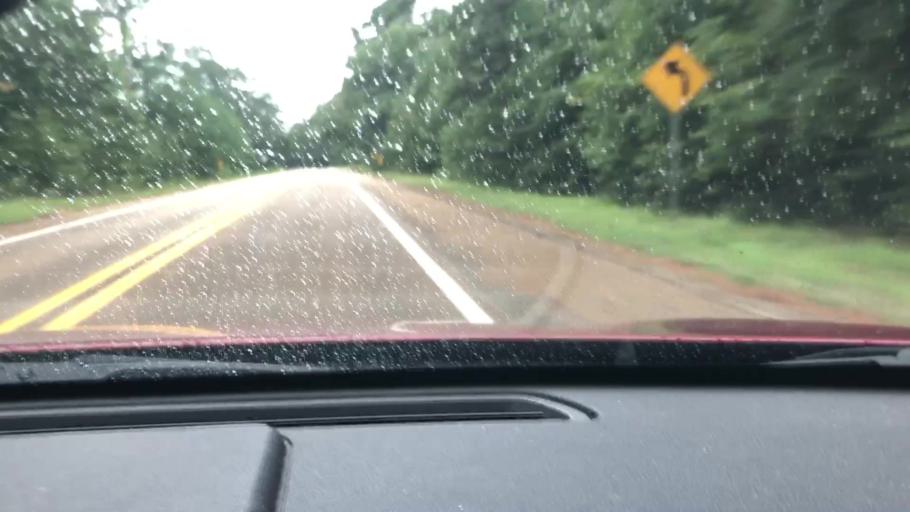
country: US
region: Arkansas
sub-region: Lafayette County
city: Stamps
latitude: 33.3559
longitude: -93.4027
